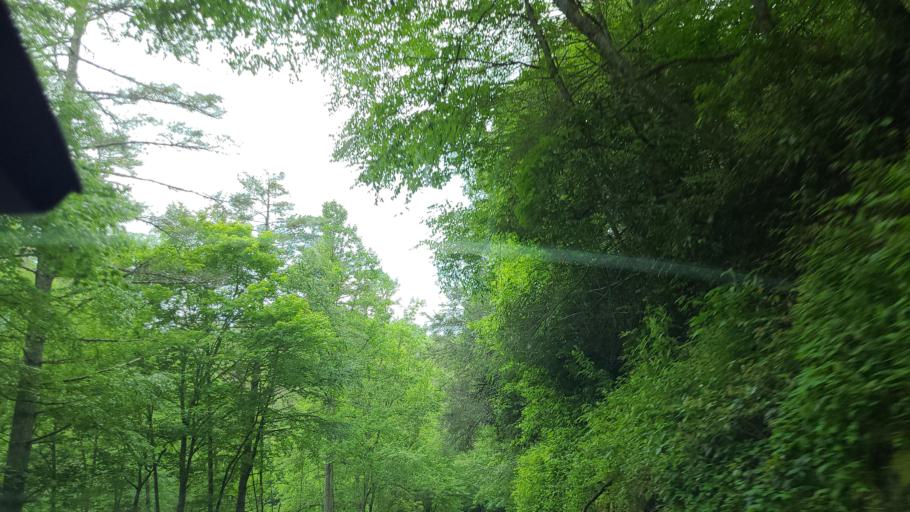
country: US
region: North Carolina
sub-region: Macon County
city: Franklin
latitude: 35.0815
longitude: -83.2589
